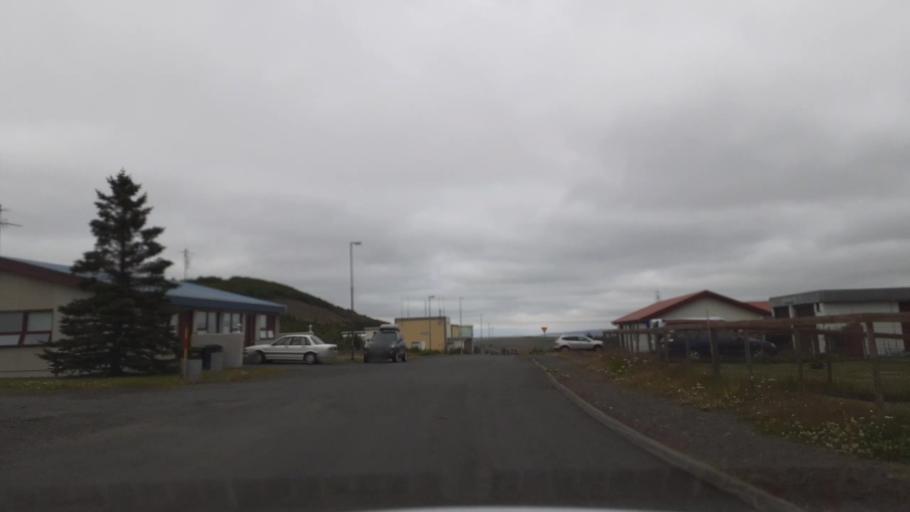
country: IS
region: Northwest
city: Saudarkrokur
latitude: 65.5504
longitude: -19.4480
